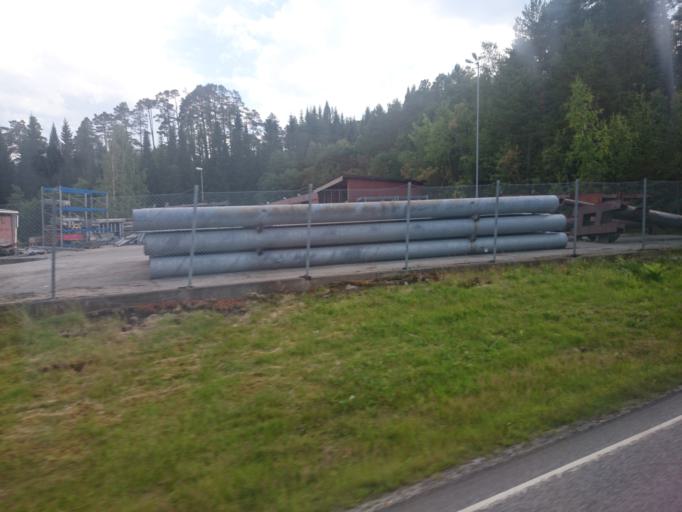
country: NO
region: More og Romsdal
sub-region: Skodje
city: Skodje
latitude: 62.4916
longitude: 6.7189
